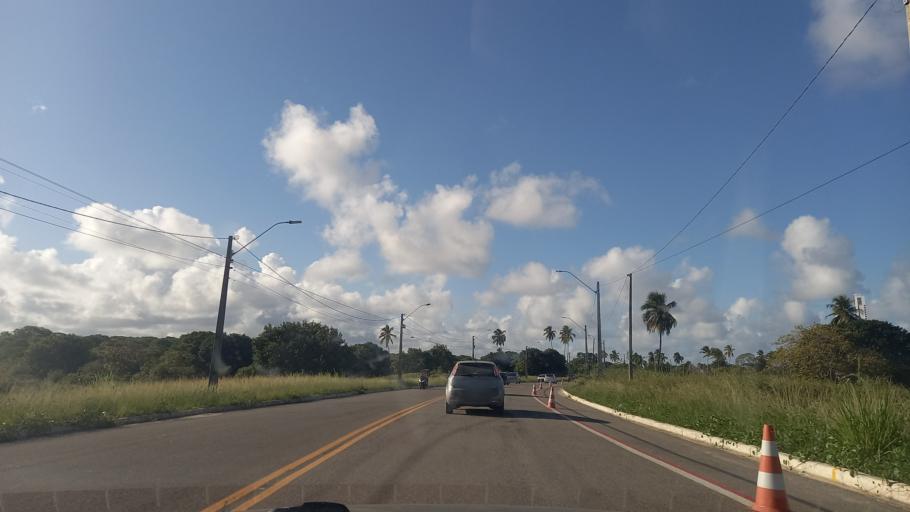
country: BR
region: Pernambuco
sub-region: Jaboatao Dos Guararapes
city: Jaboatao
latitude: -8.2342
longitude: -34.9369
